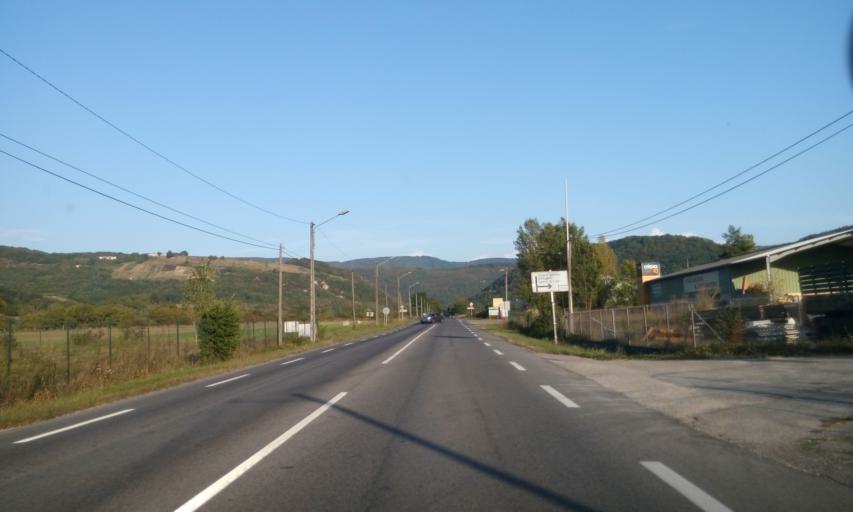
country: FR
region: Rhone-Alpes
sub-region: Departement de l'Ain
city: Poncin
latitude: 46.0812
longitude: 5.4134
